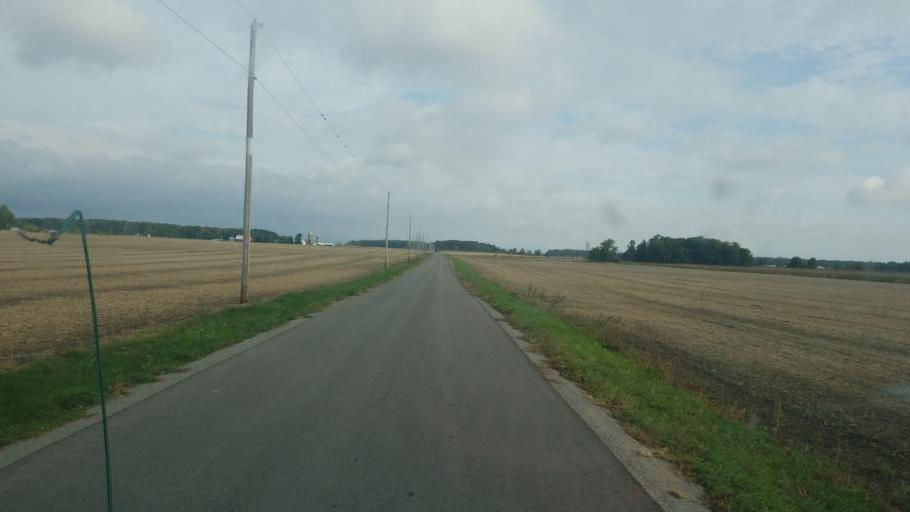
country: US
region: Ohio
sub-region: Wyandot County
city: Carey
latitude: 41.0221
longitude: -83.4487
